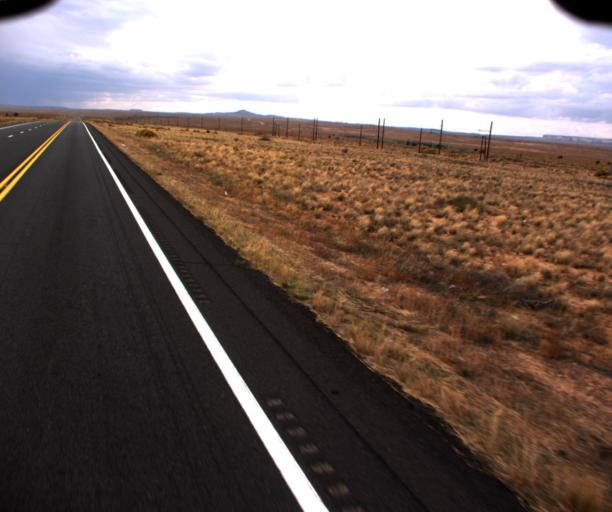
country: US
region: Arizona
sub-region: Coconino County
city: Kaibito
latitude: 36.4014
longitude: -110.8531
